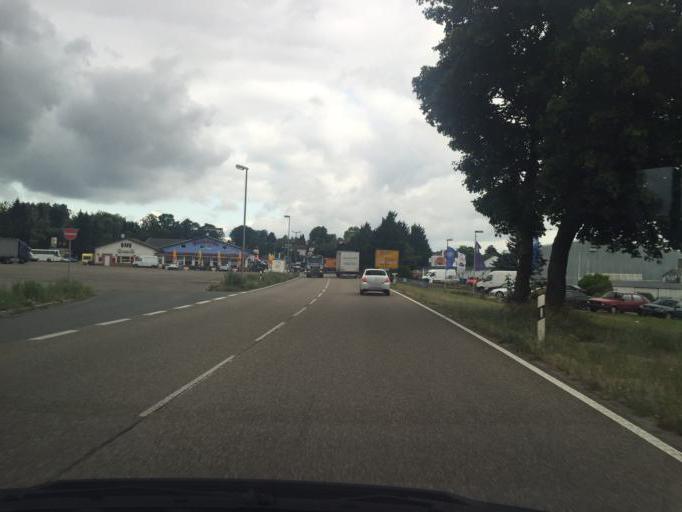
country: DE
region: Baden-Wuerttemberg
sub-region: Karlsruhe Region
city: Gondelsheim
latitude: 49.0946
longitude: 8.6439
